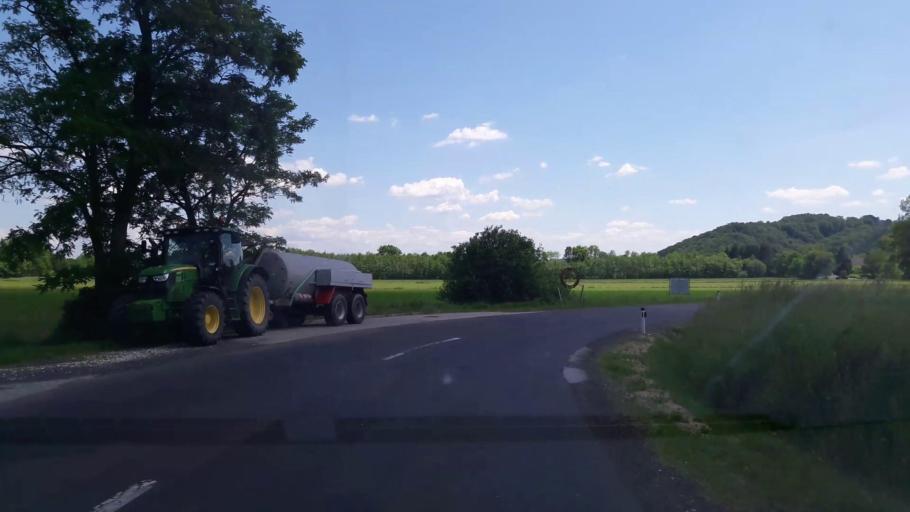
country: AT
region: Burgenland
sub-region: Politischer Bezirk Jennersdorf
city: Jennersdorf
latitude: 46.9559
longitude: 16.1178
